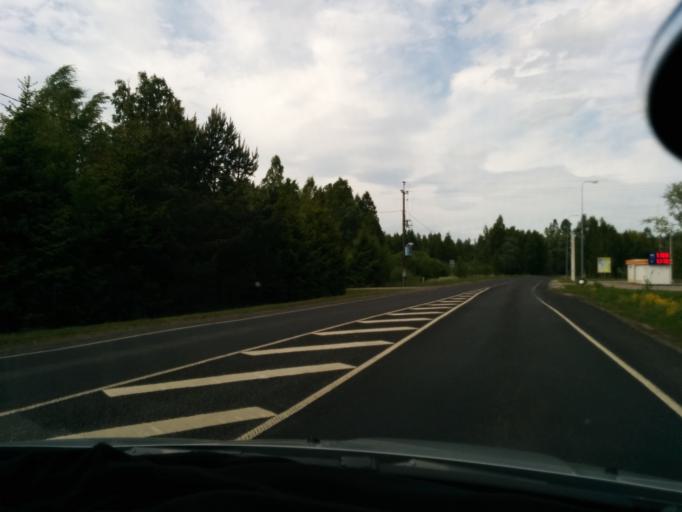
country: EE
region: Harju
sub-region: Loksa linn
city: Loksa
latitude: 59.5687
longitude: 25.7253
